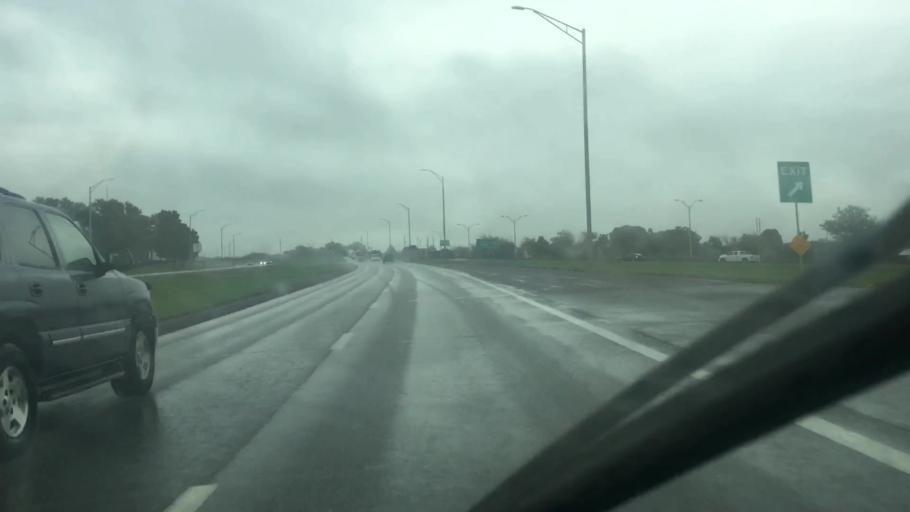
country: US
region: Kansas
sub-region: Johnson County
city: Shawnee
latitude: 39.0082
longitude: -94.7691
